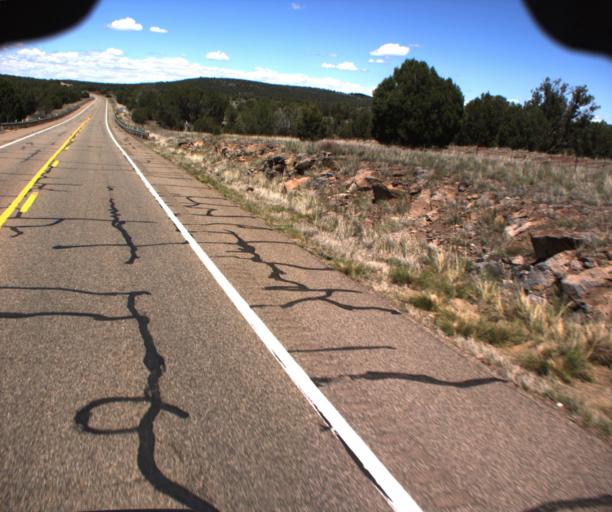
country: US
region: Arizona
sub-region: Yavapai County
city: Paulden
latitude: 35.1200
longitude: -112.4342
